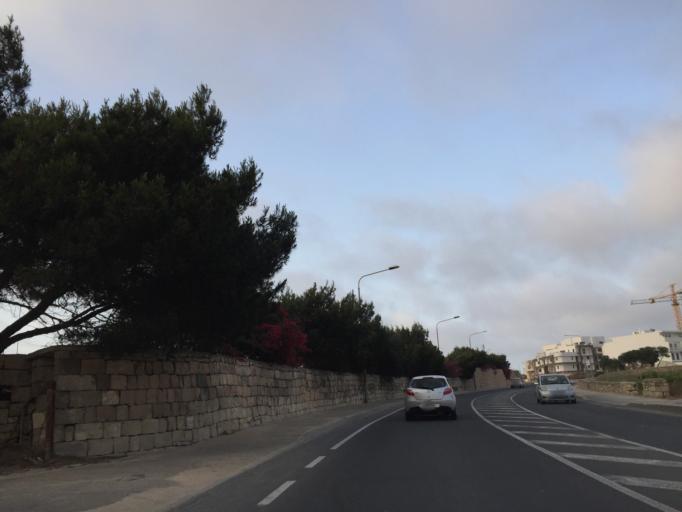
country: MT
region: Il-Mosta
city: Mosta
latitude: 35.9100
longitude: 14.4113
